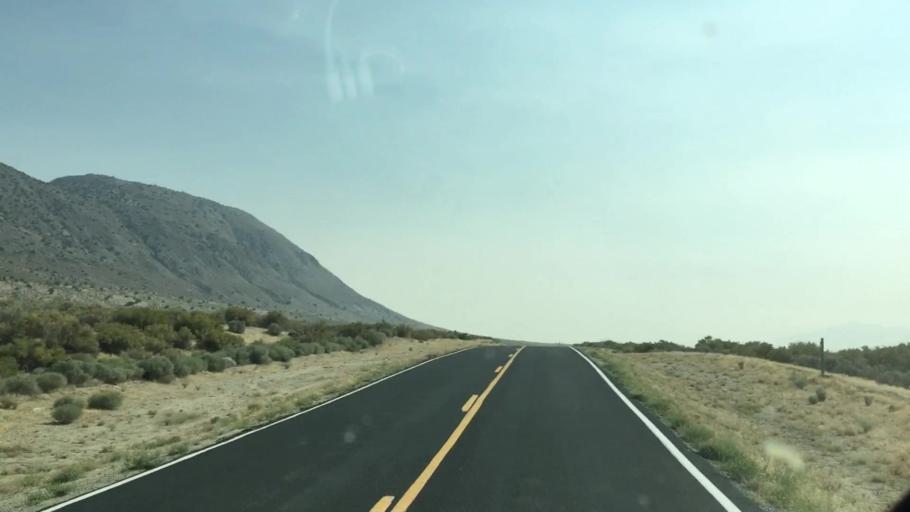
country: US
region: Nevada
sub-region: Pershing County
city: Lovelock
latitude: 40.7186
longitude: -119.3316
